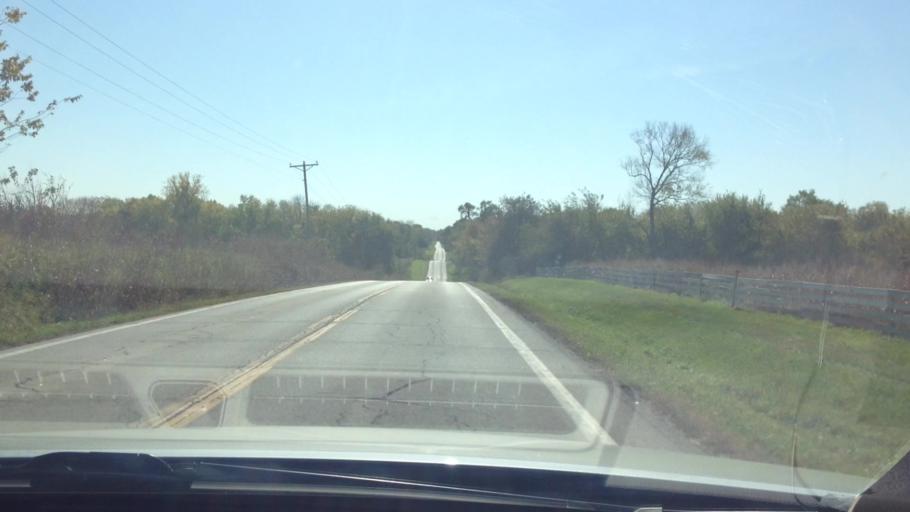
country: US
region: Missouri
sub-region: Clay County
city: Smithville
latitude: 39.3228
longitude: -94.6488
